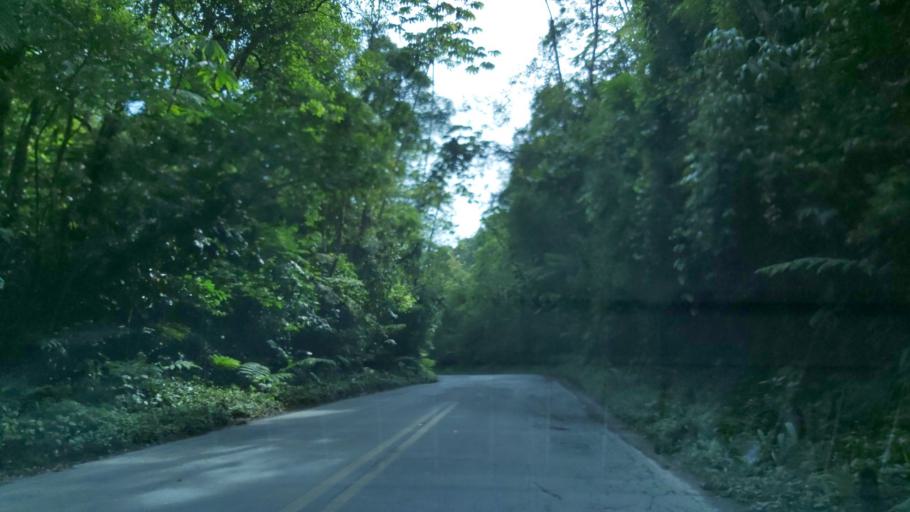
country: BR
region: Sao Paulo
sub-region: Miracatu
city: Miracatu
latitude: -24.0331
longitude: -47.5599
